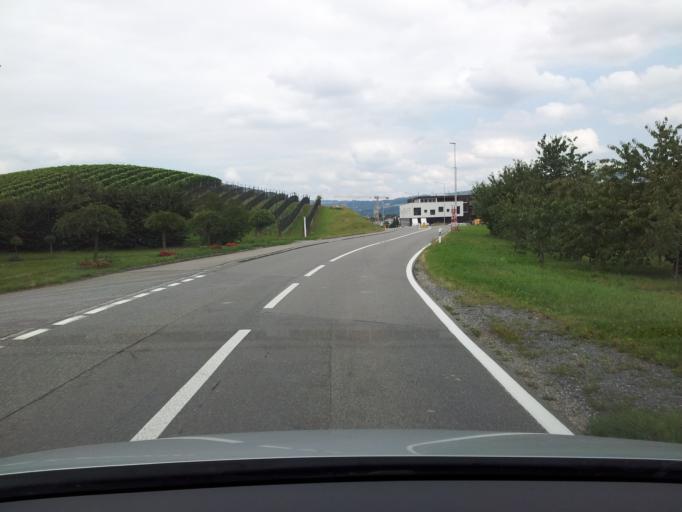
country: CH
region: Lucerne
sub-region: Sursee District
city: Oberkirch
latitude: 47.1500
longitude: 8.1147
